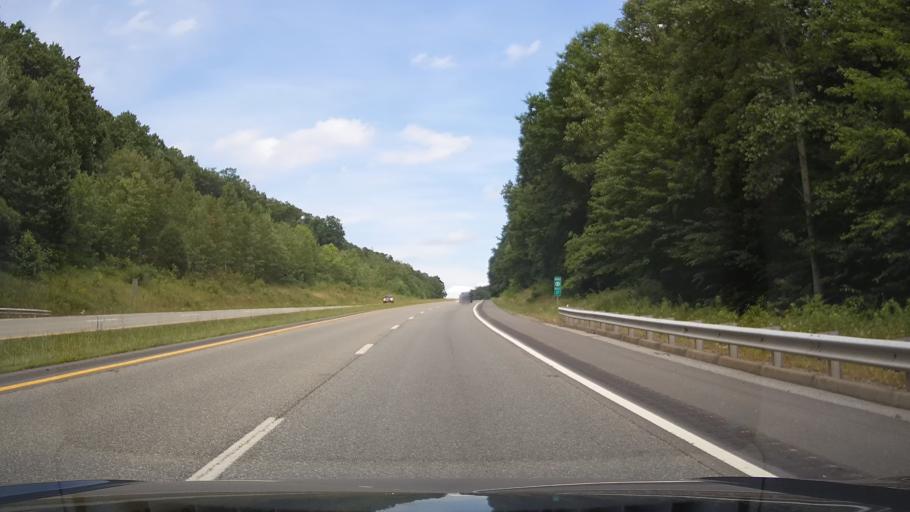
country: US
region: Virginia
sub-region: Wise County
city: Big Stone Gap
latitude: 36.8962
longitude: -82.7078
